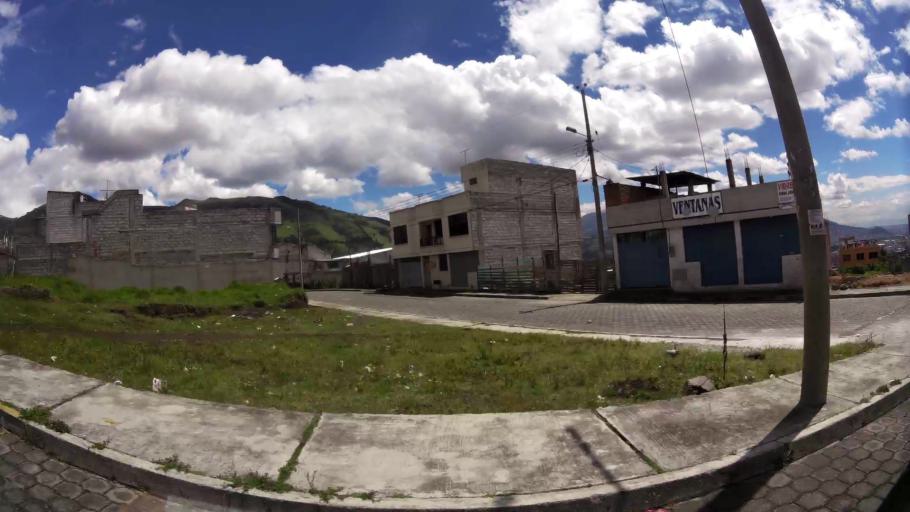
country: EC
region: Pichincha
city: Quito
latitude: -0.3332
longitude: -78.5636
